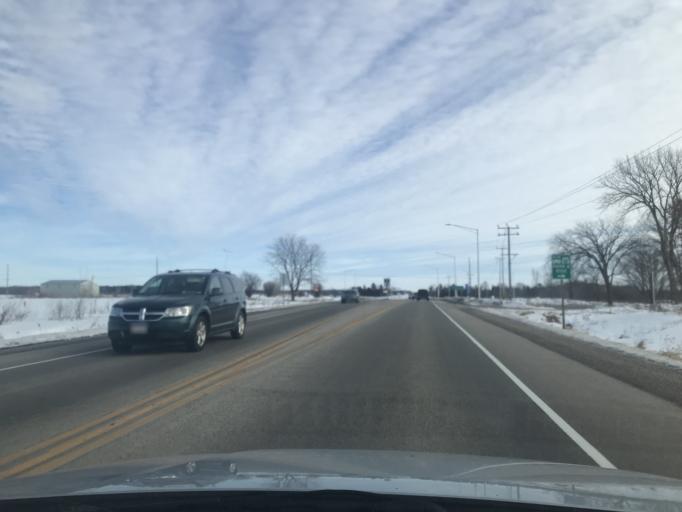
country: US
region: Wisconsin
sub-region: Oconto County
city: Gillett
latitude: 44.8961
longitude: -88.2496
